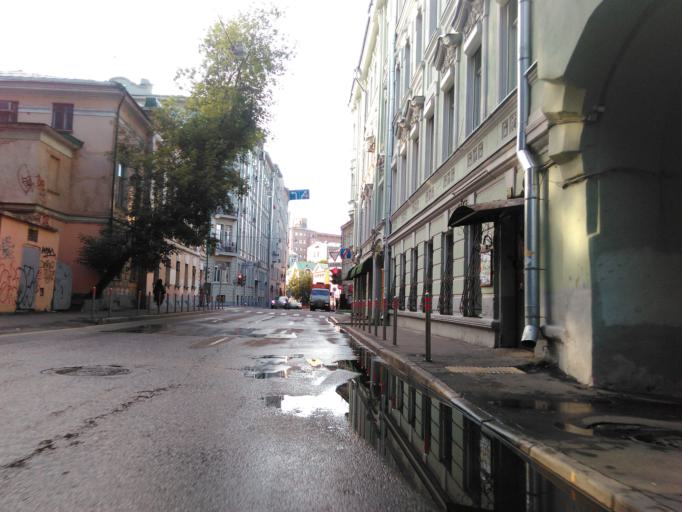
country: RU
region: Moscow
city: Taganskiy
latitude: 55.7592
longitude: 37.6520
